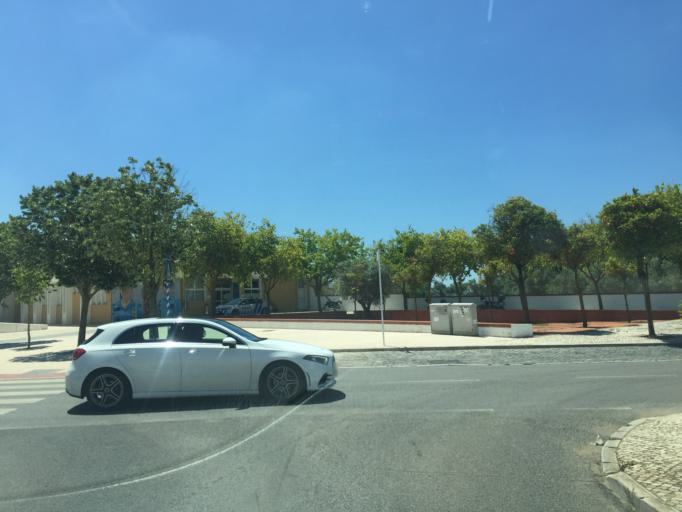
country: PT
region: Lisbon
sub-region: Oeiras
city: Quejas
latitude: 38.7207
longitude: -9.2637
